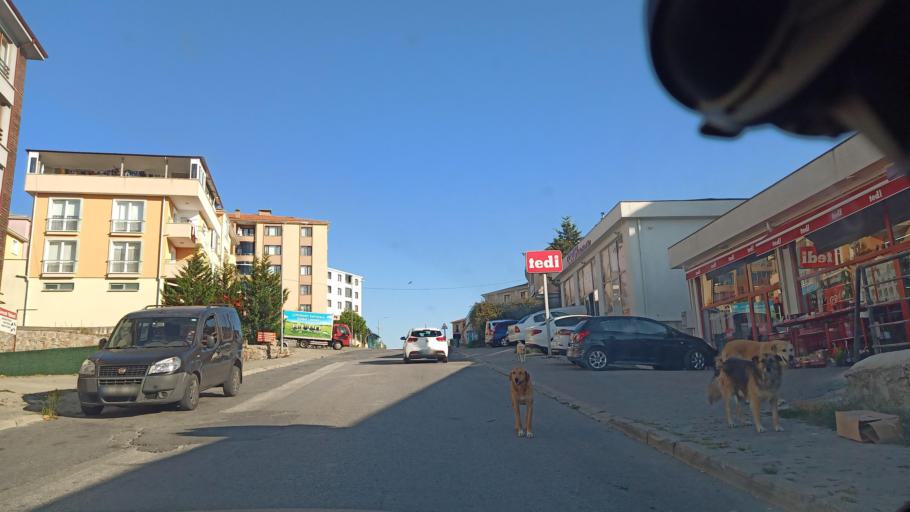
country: TR
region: Kocaeli
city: Kaymaz
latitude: 40.8596
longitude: 30.2884
